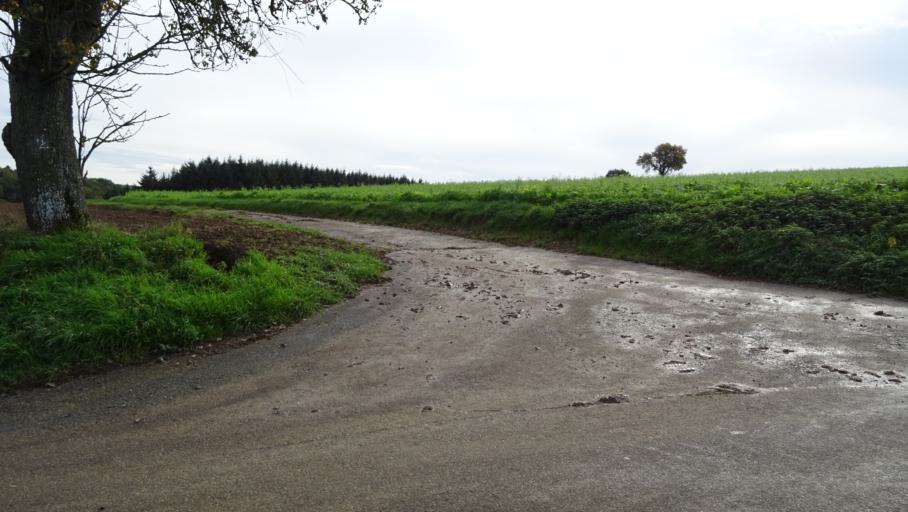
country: DE
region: Baden-Wuerttemberg
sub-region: Karlsruhe Region
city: Billigheim
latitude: 49.3376
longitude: 9.2233
